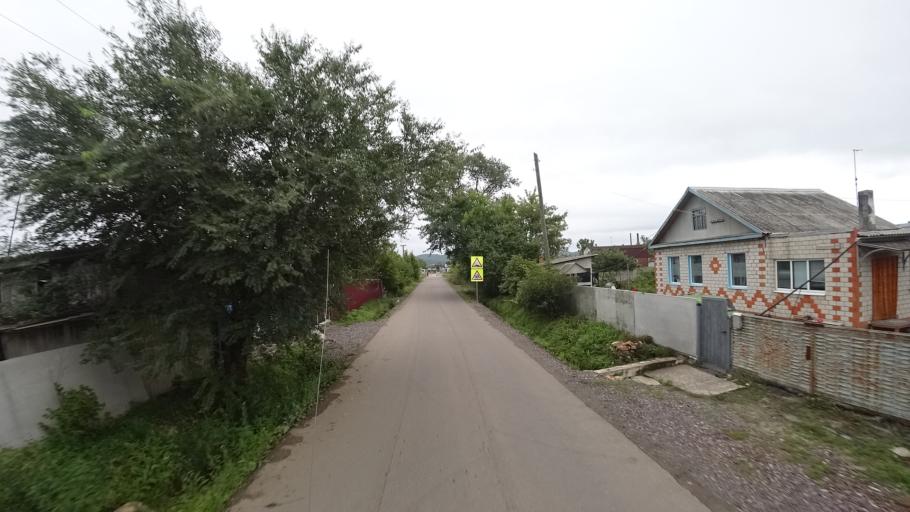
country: RU
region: Primorskiy
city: Chernigovka
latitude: 44.3364
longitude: 132.5403
